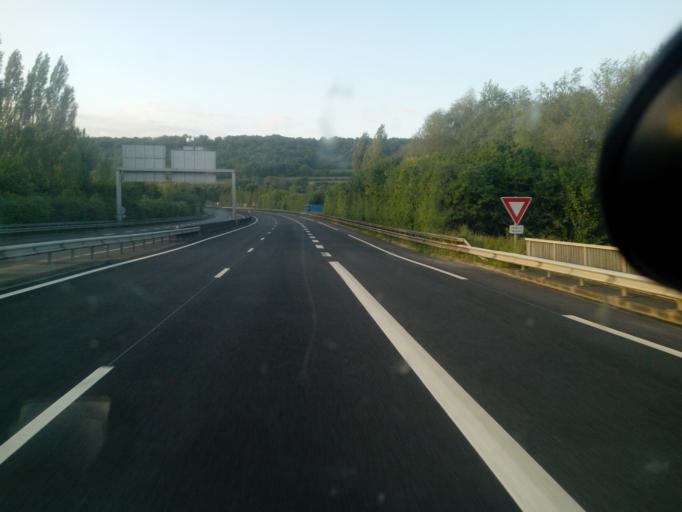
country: FR
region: Picardie
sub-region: Departement de la Somme
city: Bouttencourt
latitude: 49.9289
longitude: 1.6420
